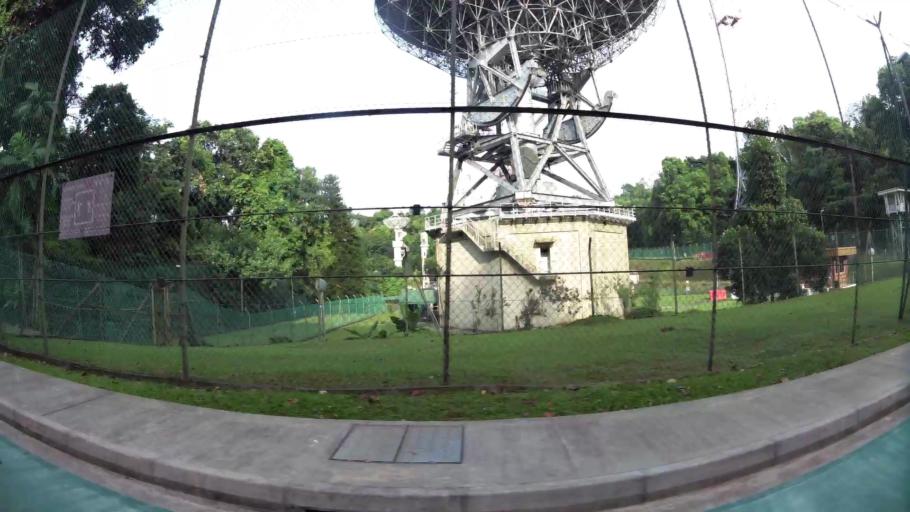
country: SG
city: Singapore
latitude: 1.2472
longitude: 103.8371
